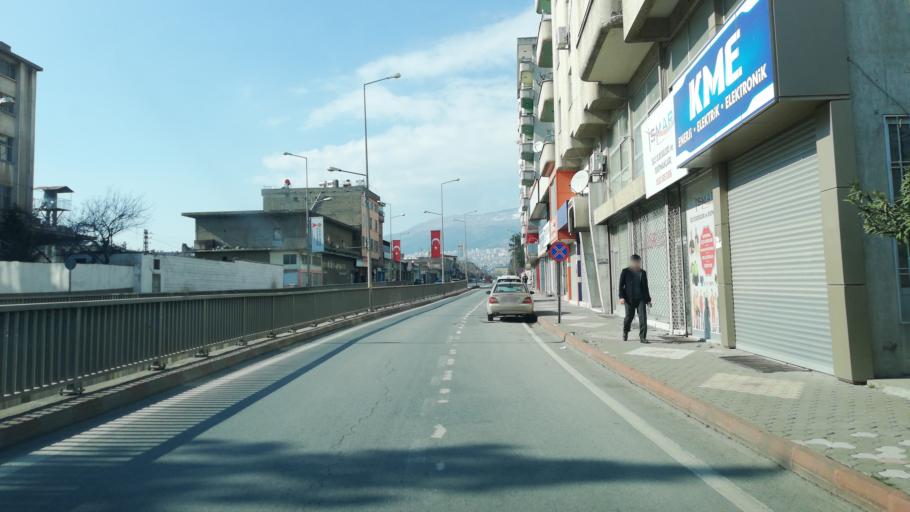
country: TR
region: Kahramanmaras
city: Kahramanmaras
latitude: 37.5718
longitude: 36.9416
